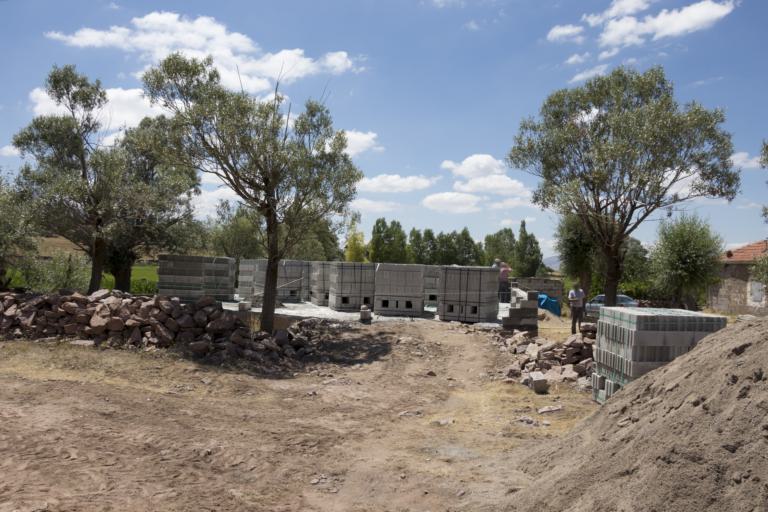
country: TR
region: Kayseri
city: Toklar
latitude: 38.4247
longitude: 36.0965
